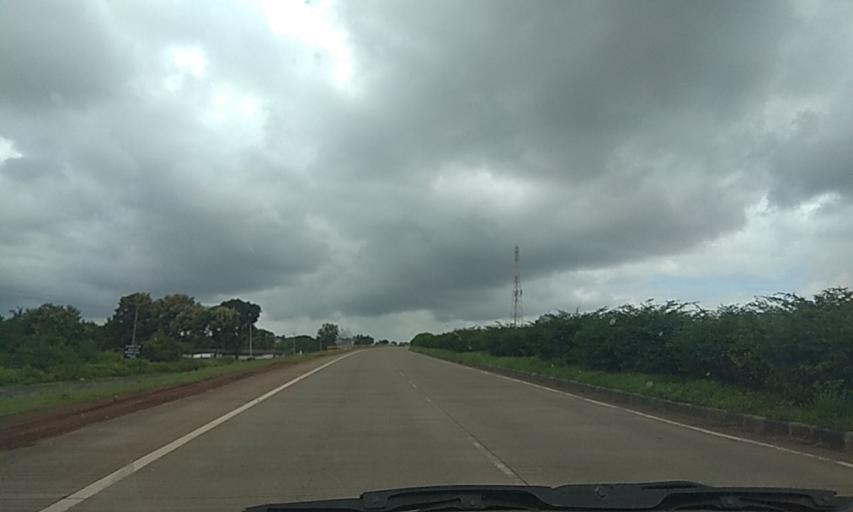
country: IN
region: Karnataka
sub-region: Belgaum
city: Sankeshwar
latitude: 16.2520
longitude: 74.4741
